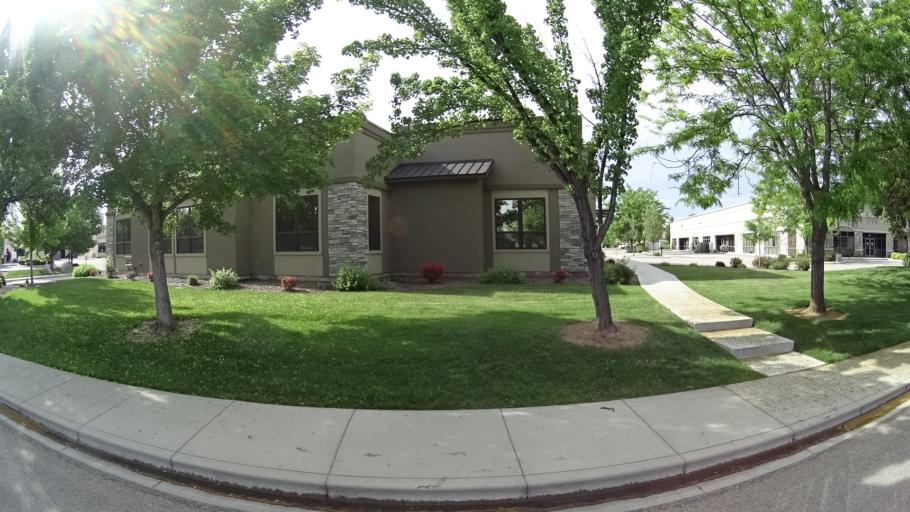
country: US
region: Idaho
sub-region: Ada County
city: Meridian
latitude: 43.5836
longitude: -116.3534
